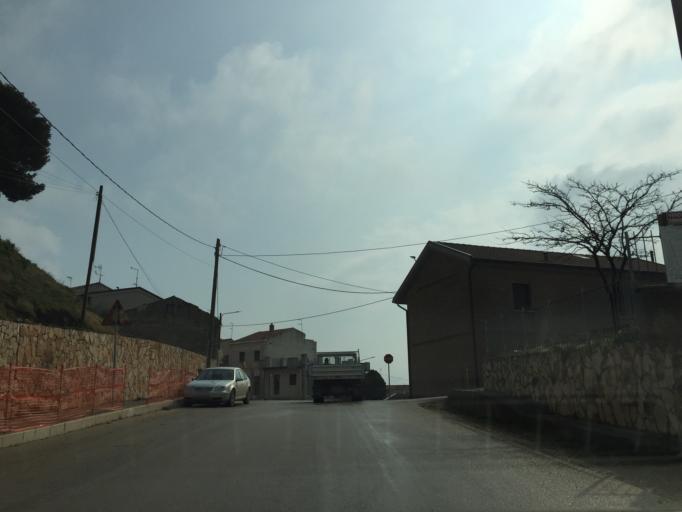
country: IT
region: Apulia
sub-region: Provincia di Foggia
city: Troia
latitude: 41.3587
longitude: 15.3019
